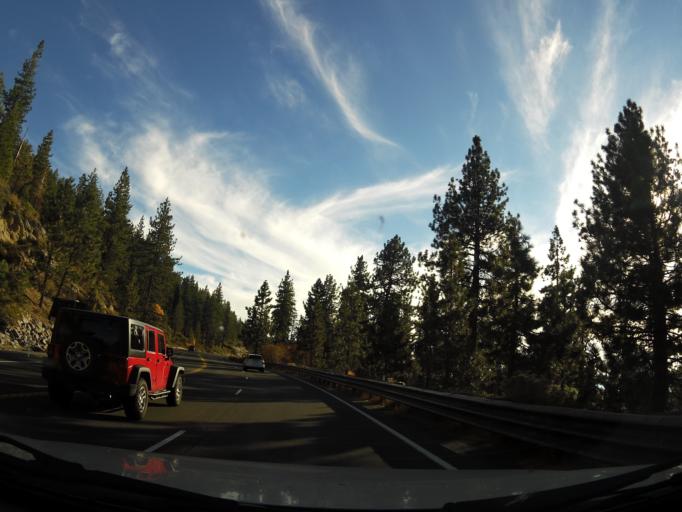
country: US
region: Nevada
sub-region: Douglas County
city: Kingsbury
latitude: 39.0608
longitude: -119.9427
